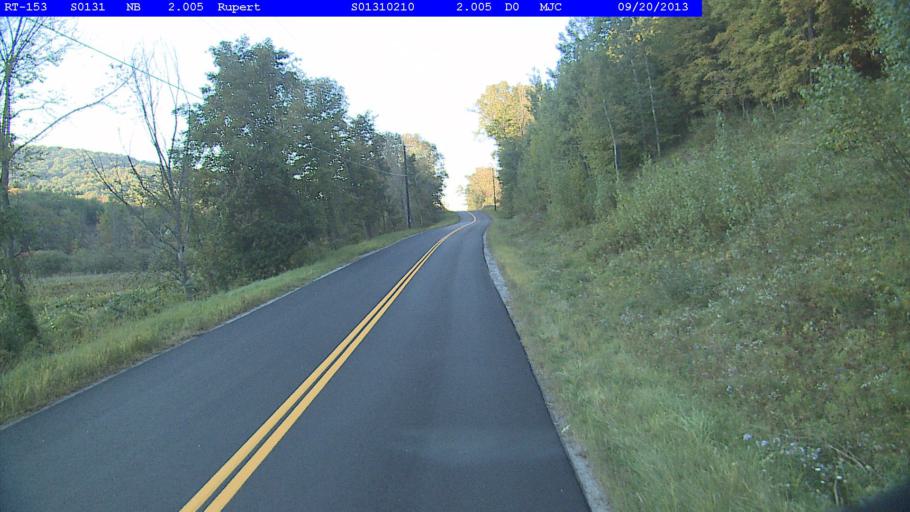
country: US
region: New York
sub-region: Washington County
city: Granville
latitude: 43.2839
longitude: -73.2382
